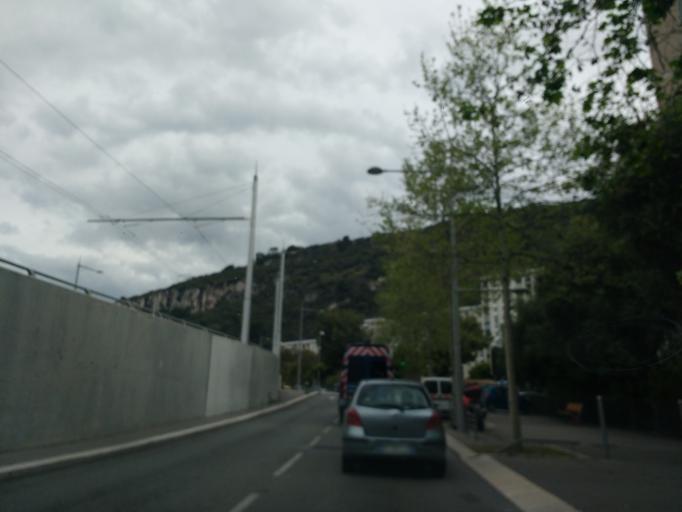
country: FR
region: Provence-Alpes-Cote d'Azur
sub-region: Departement des Alpes-Maritimes
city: Saint-Andre-de-la-Roche
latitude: 43.7222
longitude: 7.2920
